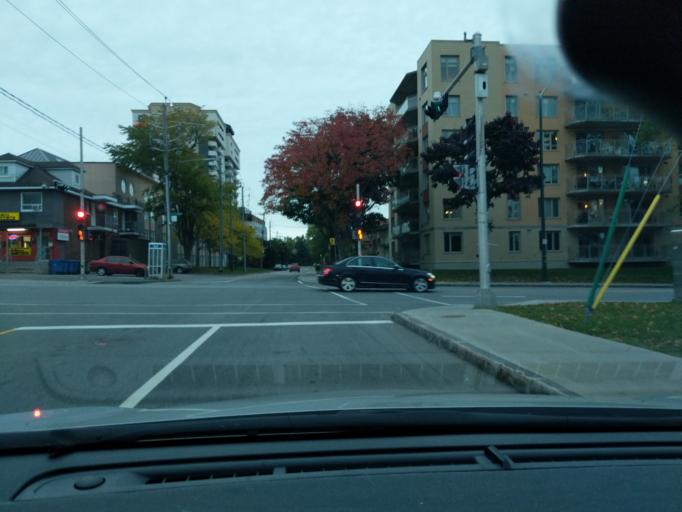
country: CA
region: Quebec
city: L'Ancienne-Lorette
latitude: 46.7661
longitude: -71.2880
